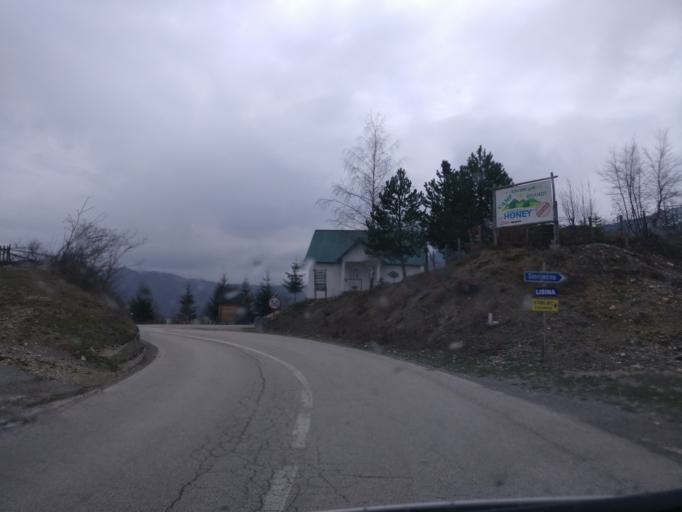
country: ME
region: Opstina Pluzine
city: Pluzine
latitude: 43.1266
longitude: 18.8133
